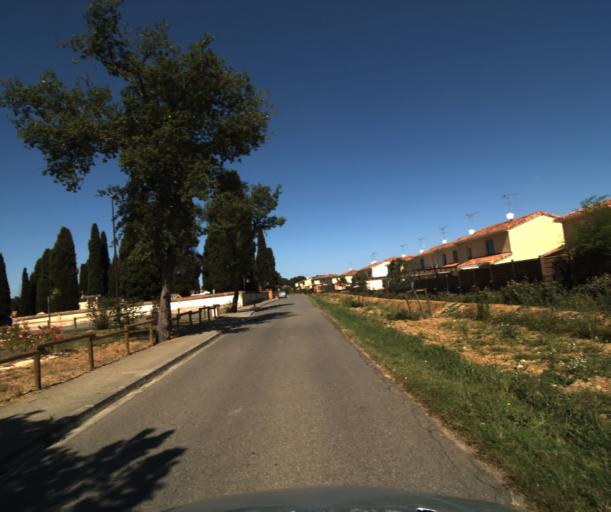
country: FR
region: Midi-Pyrenees
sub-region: Departement de la Haute-Garonne
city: Eaunes
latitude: 43.4220
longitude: 1.3528
